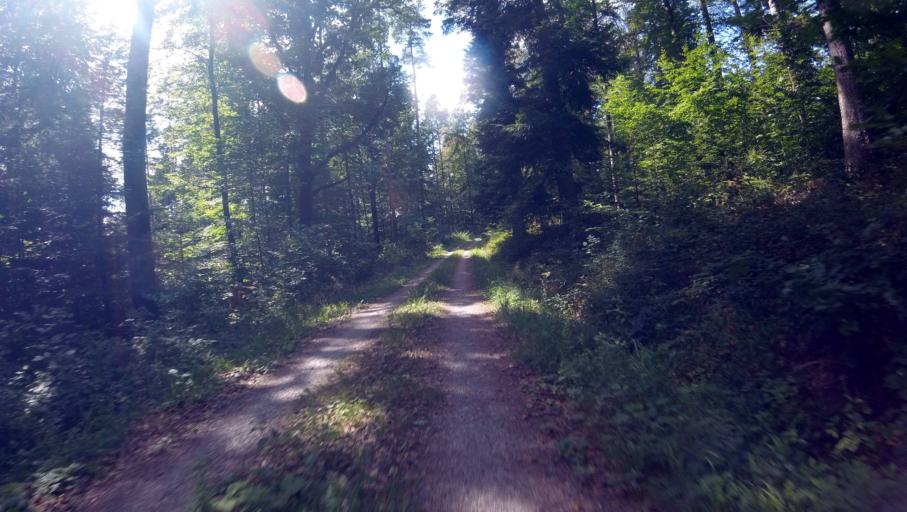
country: DE
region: Baden-Wuerttemberg
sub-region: Regierungsbezirk Stuttgart
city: Aspach
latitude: 49.0129
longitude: 9.3997
